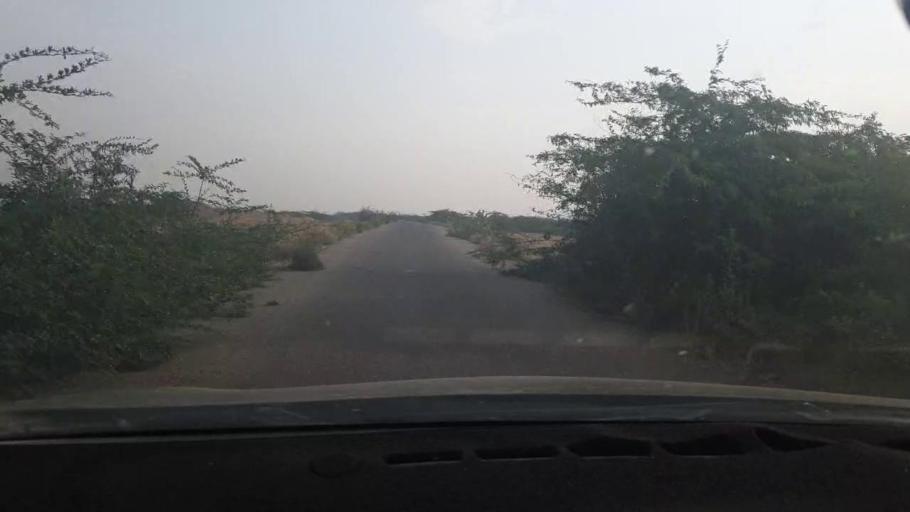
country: PK
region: Sindh
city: Malir Cantonment
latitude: 24.9514
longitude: 67.4367
